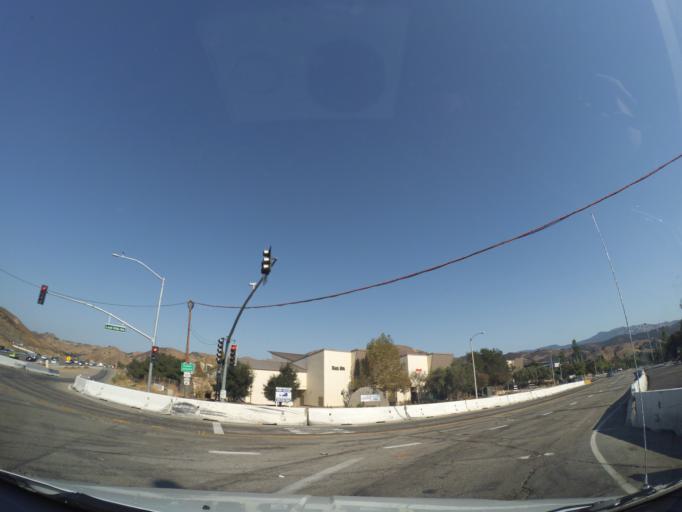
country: US
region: California
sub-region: Los Angeles County
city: Agoura
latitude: 34.1403
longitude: -118.7094
